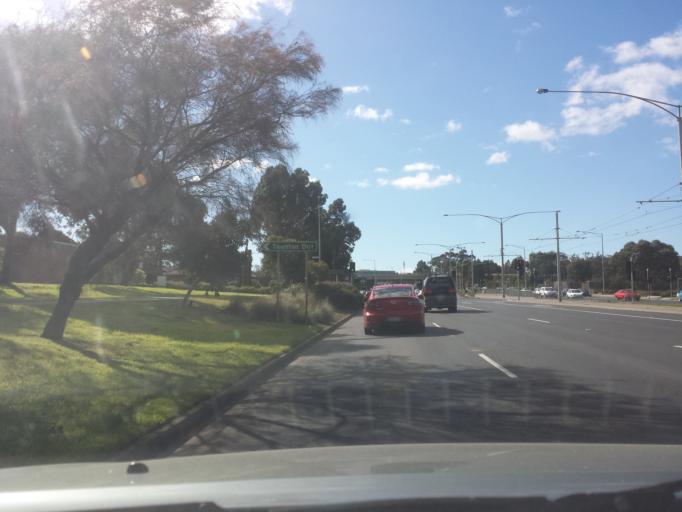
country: AU
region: Victoria
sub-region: Banyule
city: Bundoora
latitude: -37.6888
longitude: 145.0657
